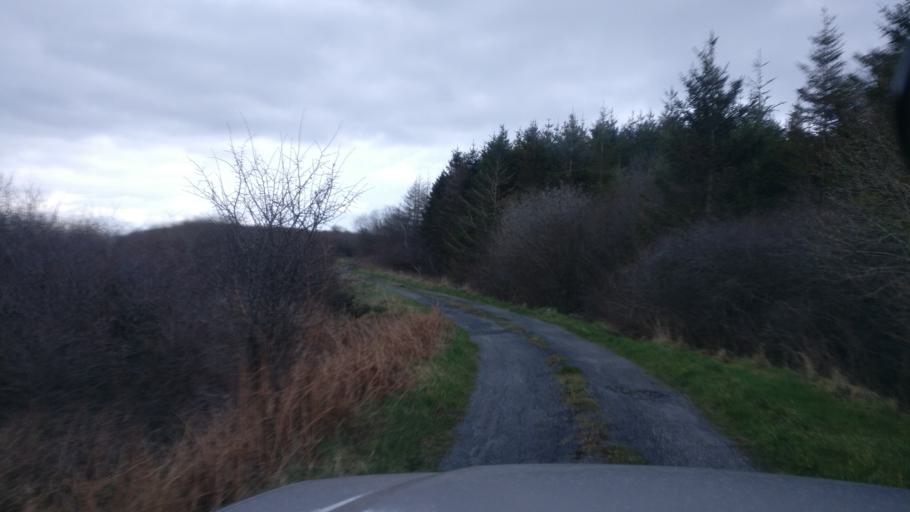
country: IE
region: Connaught
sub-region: County Galway
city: Loughrea
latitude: 53.2738
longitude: -8.4598
